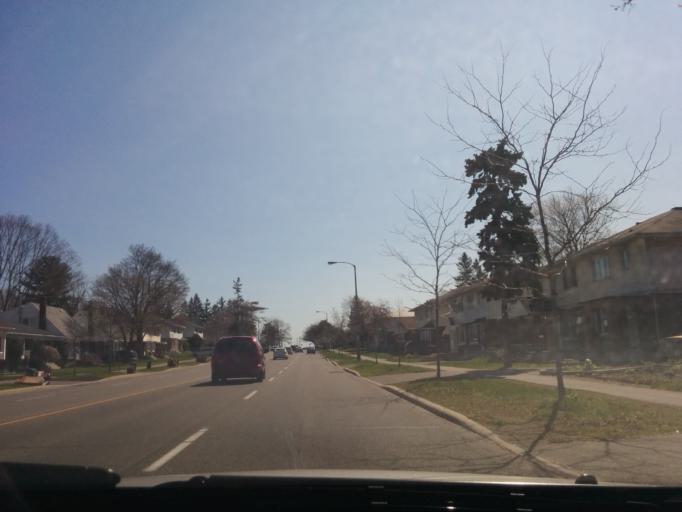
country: CA
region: Ontario
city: Ottawa
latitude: 45.4005
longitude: -75.6316
